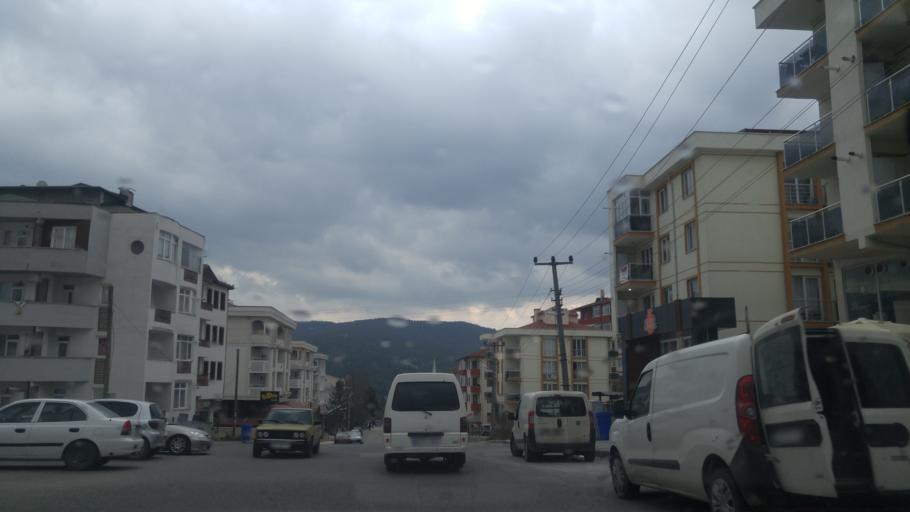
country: TR
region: Karabuk
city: Safranbolu
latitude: 41.2208
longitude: 32.6726
